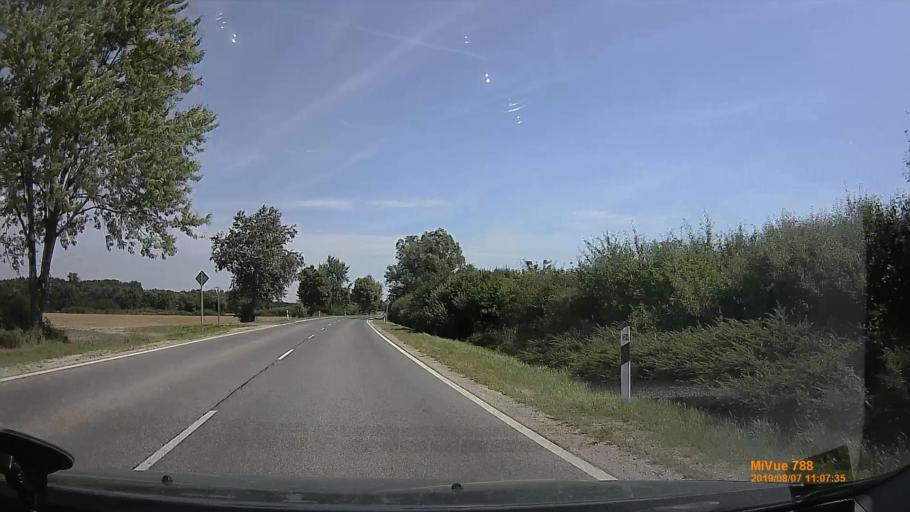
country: SI
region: Lendava-Lendva
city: Lendava
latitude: 46.6251
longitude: 16.4677
